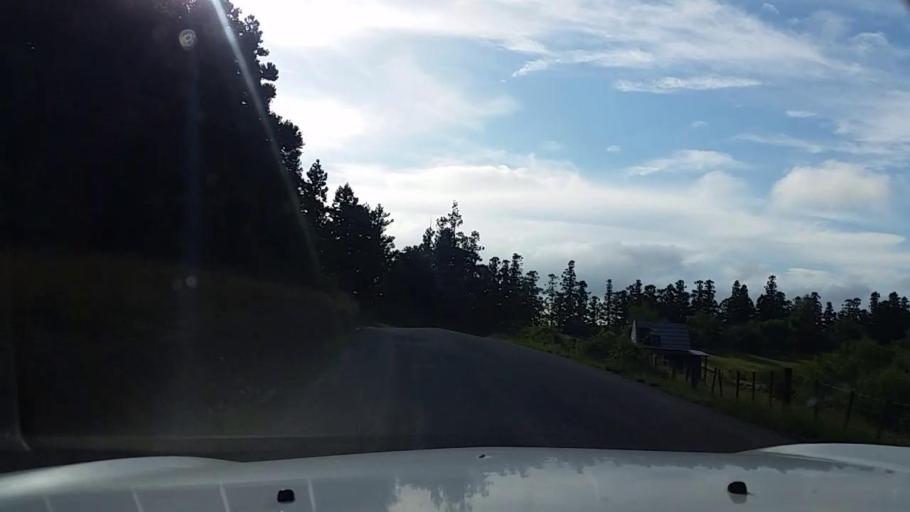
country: NZ
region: Northland
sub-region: Whangarei
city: Maungatapere
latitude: -35.6774
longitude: 174.1773
